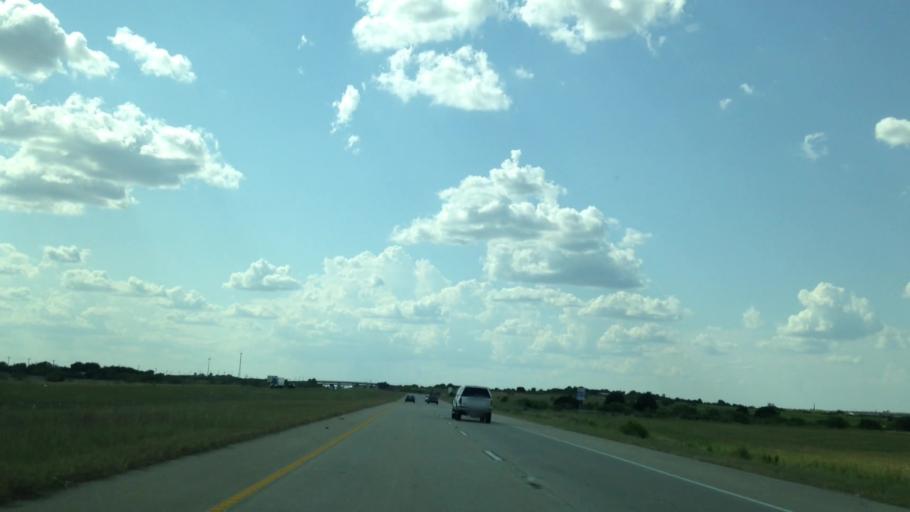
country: US
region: Texas
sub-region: Travis County
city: Onion Creek
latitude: 30.0873
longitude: -97.7425
